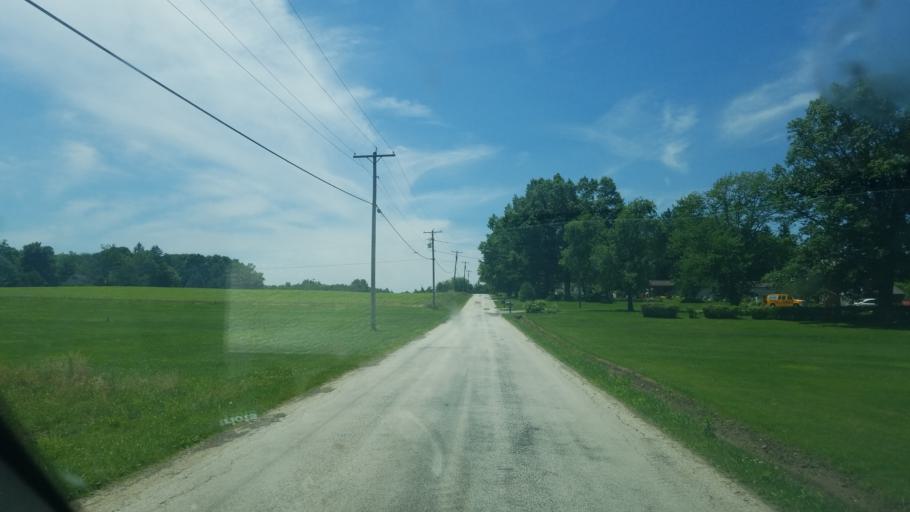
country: US
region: Ohio
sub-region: Stark County
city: Alliance
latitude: 40.8578
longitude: -81.0822
